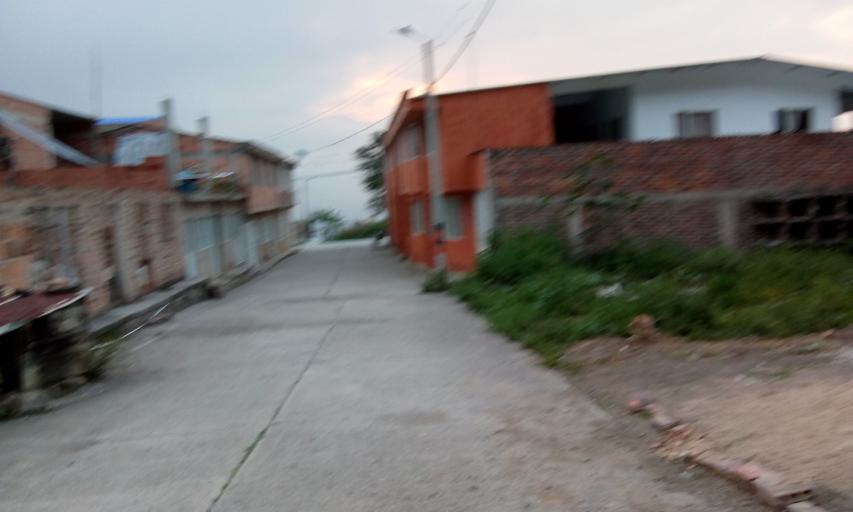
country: CO
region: Boyaca
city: Tipacoque
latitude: 6.4199
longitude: -72.6936
